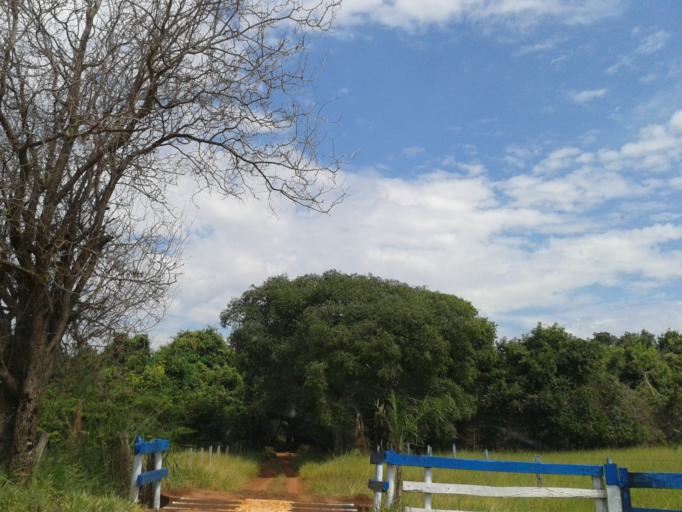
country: BR
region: Minas Gerais
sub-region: Campina Verde
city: Campina Verde
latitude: -19.3917
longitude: -49.6355
